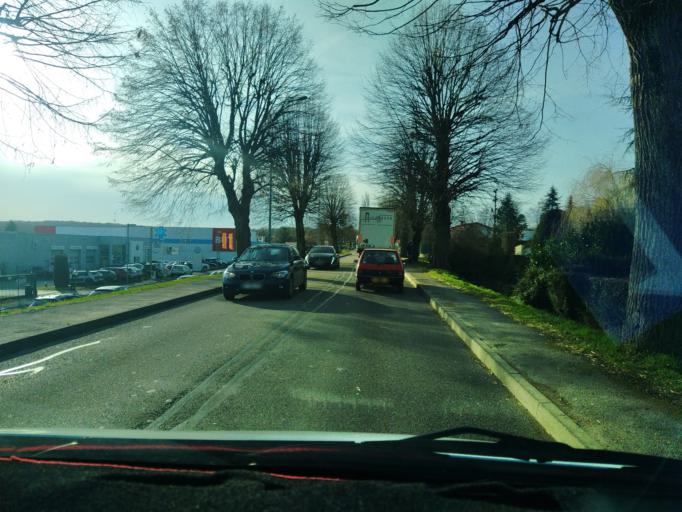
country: FR
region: Franche-Comte
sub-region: Departement de la Haute-Saone
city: Gray
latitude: 47.4382
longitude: 5.5996
